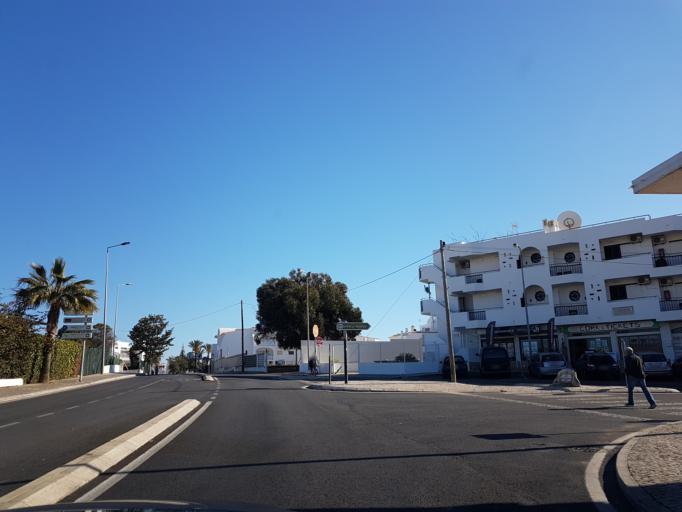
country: PT
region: Faro
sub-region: Albufeira
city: Albufeira
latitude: 37.0887
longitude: -8.2292
